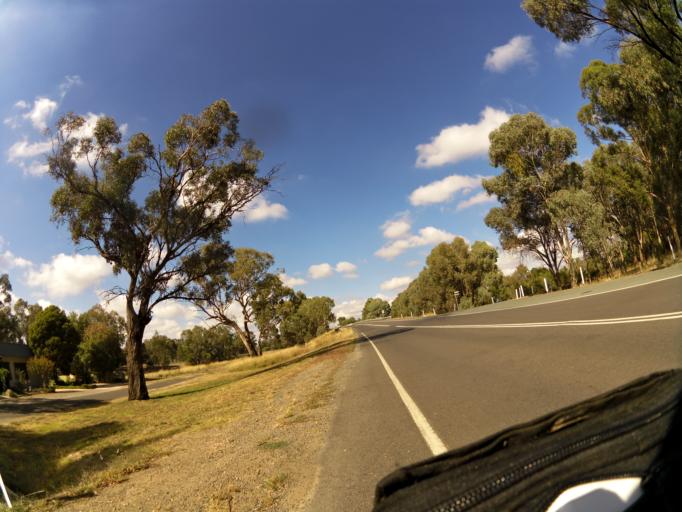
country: AU
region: Victoria
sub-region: Benalla
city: Benalla
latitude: -36.5713
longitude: 145.9921
